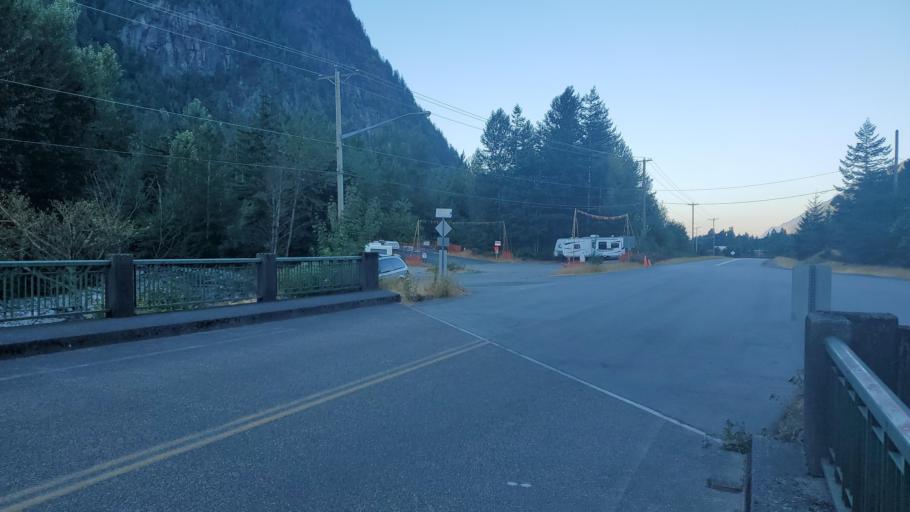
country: CA
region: British Columbia
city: Hope
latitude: 49.3558
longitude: -121.5748
